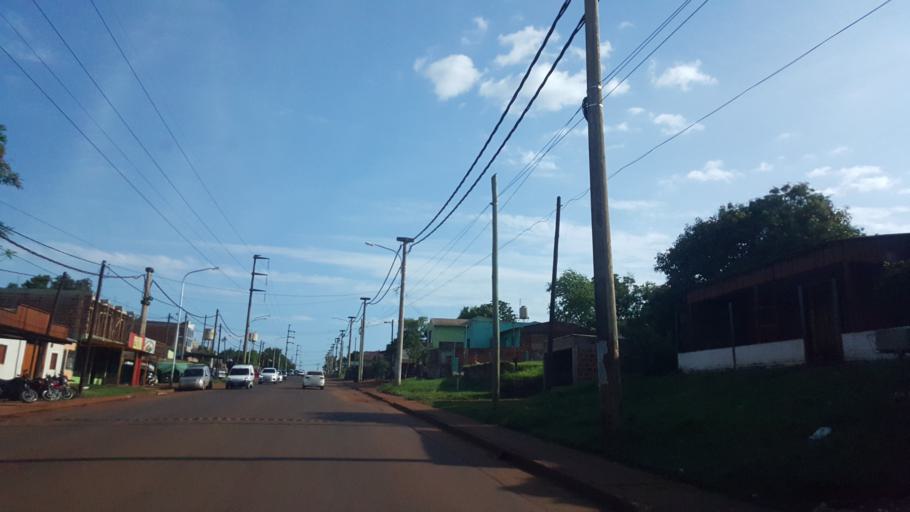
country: AR
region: Misiones
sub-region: Departamento de Capital
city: Posadas
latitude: -27.4243
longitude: -55.9138
